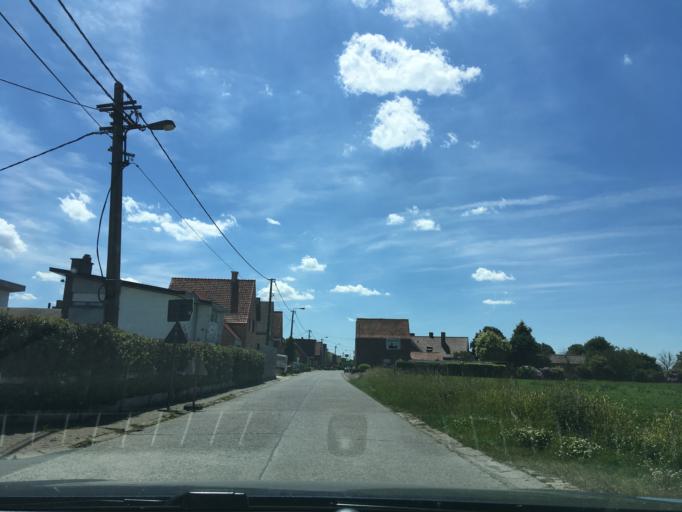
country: BE
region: Flanders
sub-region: Provincie West-Vlaanderen
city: Lichtervelde
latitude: 51.0370
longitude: 3.1330
